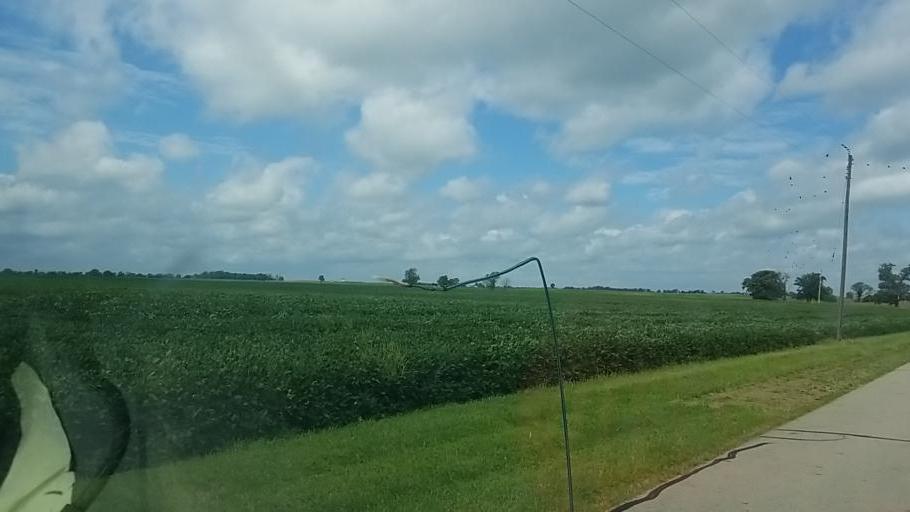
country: US
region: Ohio
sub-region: Fayette County
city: Jeffersonville
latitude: 39.6905
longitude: -83.5766
